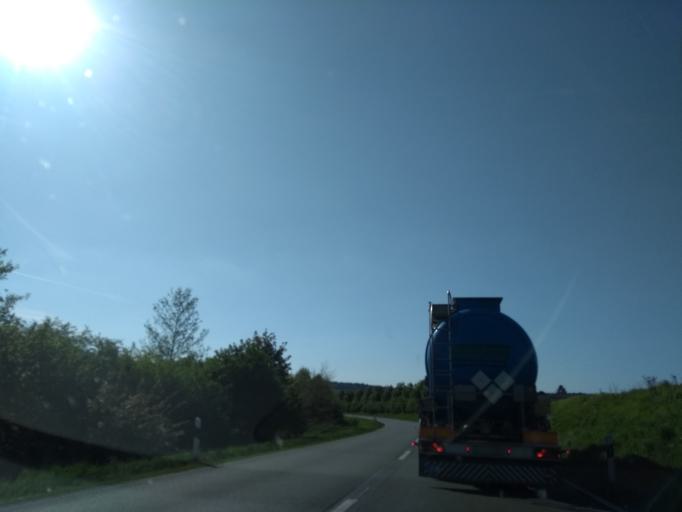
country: DE
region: Hesse
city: Frankenberg
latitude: 51.0433
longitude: 8.7511
